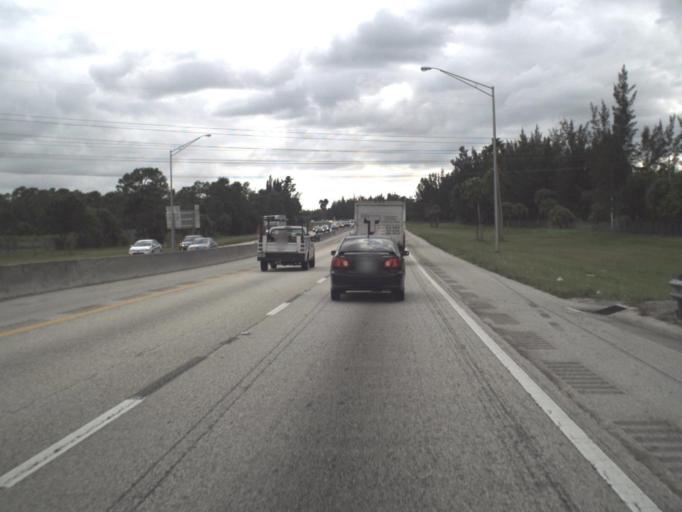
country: US
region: Florida
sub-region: Palm Beach County
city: Lake Belvedere Estates
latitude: 26.6763
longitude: -80.1686
